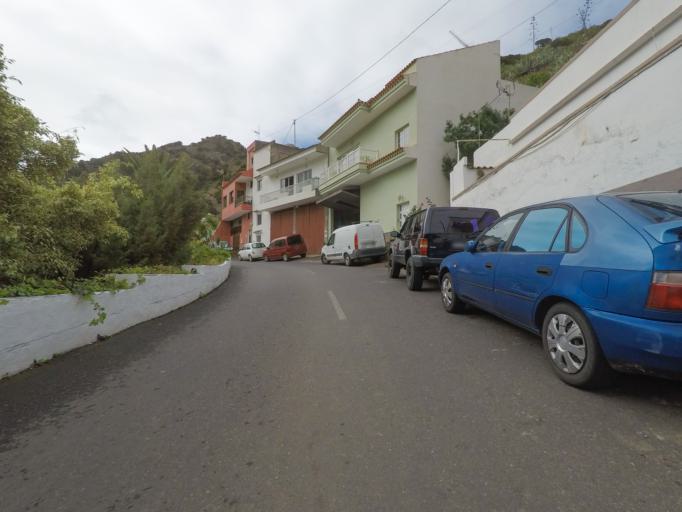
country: ES
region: Canary Islands
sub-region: Provincia de Santa Cruz de Tenerife
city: Vallehermosa
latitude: 28.1798
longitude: -17.2672
